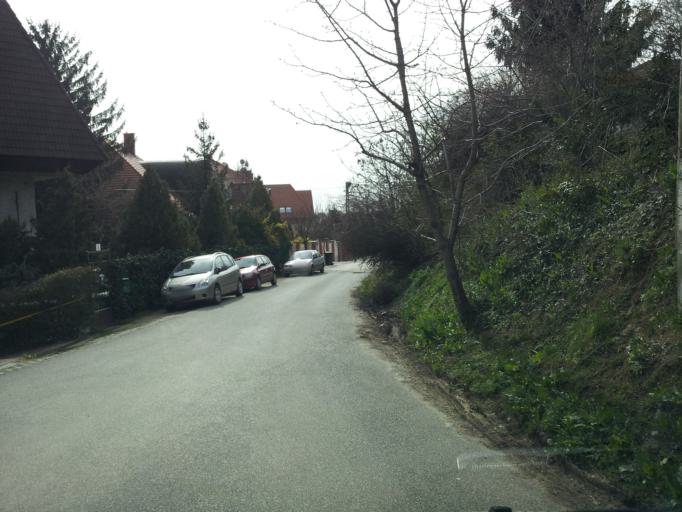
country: HU
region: Budapest
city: Budapest XII. keruelet
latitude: 47.4789
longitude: 18.9926
